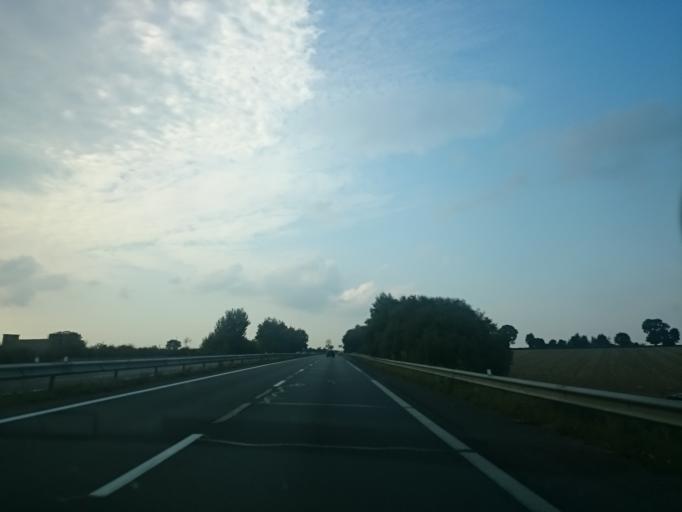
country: FR
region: Brittany
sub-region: Departement des Cotes-d'Armor
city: Plenee-Jugon
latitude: 48.3877
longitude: -2.3866
